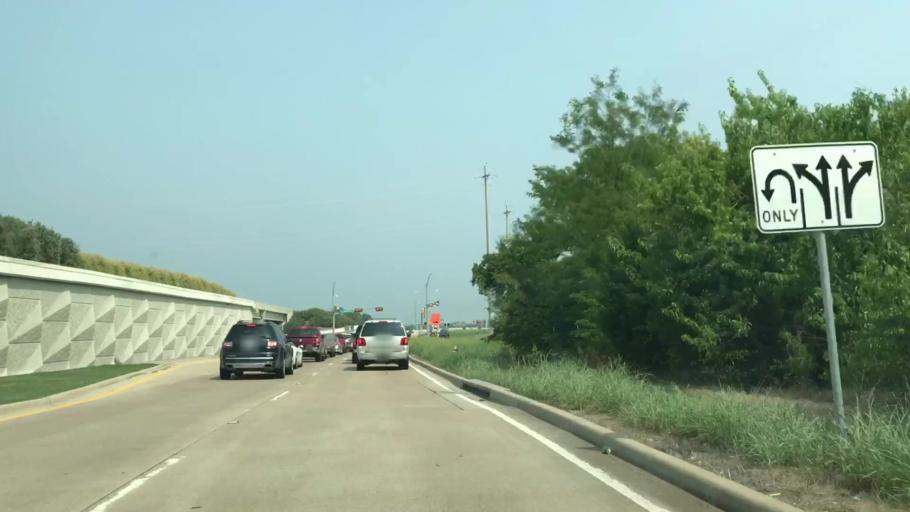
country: US
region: Texas
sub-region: Dallas County
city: Sachse
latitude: 32.9506
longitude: -96.5721
